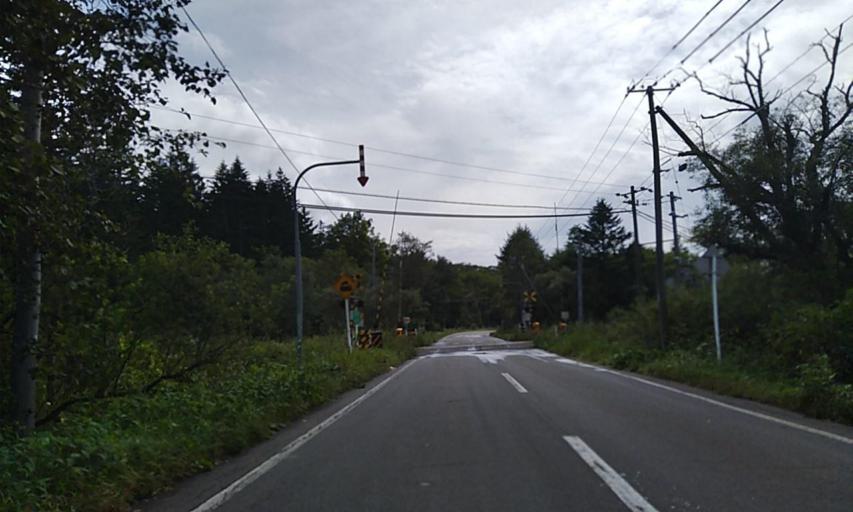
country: JP
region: Hokkaido
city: Kushiro
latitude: 42.8439
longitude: 143.8422
